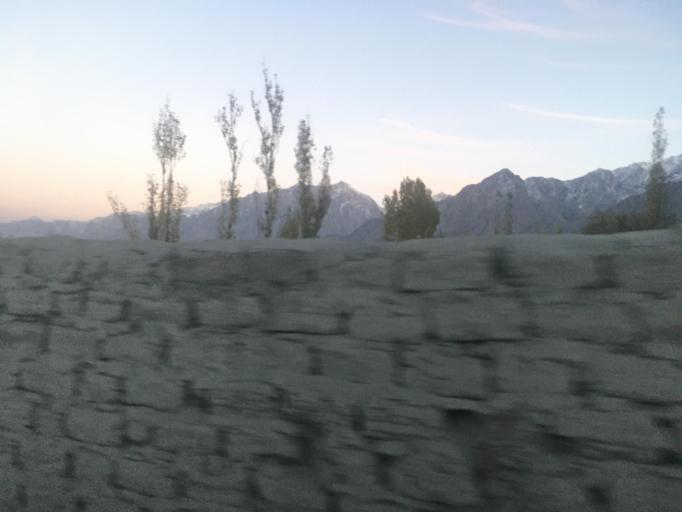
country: PK
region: Gilgit-Baltistan
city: Skardu
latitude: 35.2984
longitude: 75.5471
